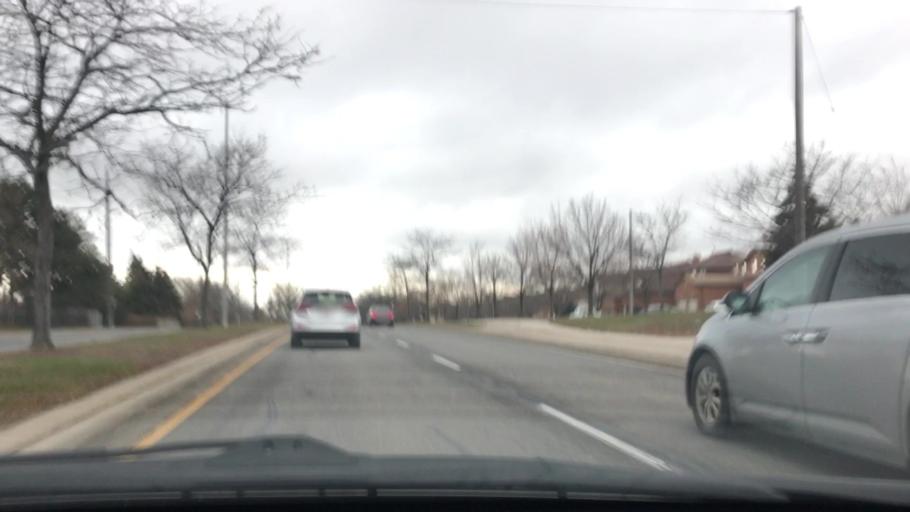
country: CA
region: Ontario
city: Oakville
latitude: 43.4883
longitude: -79.6872
